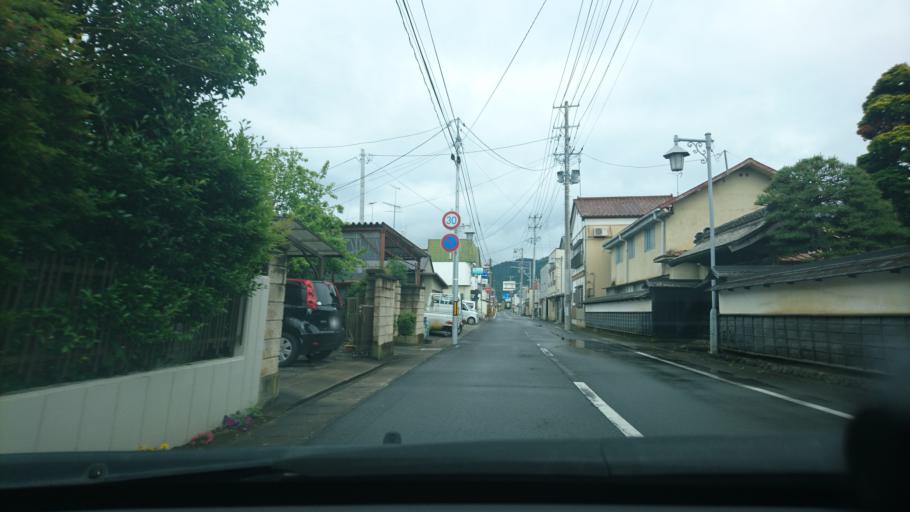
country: JP
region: Miyagi
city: Wakuya
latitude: 38.6517
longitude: 141.2785
